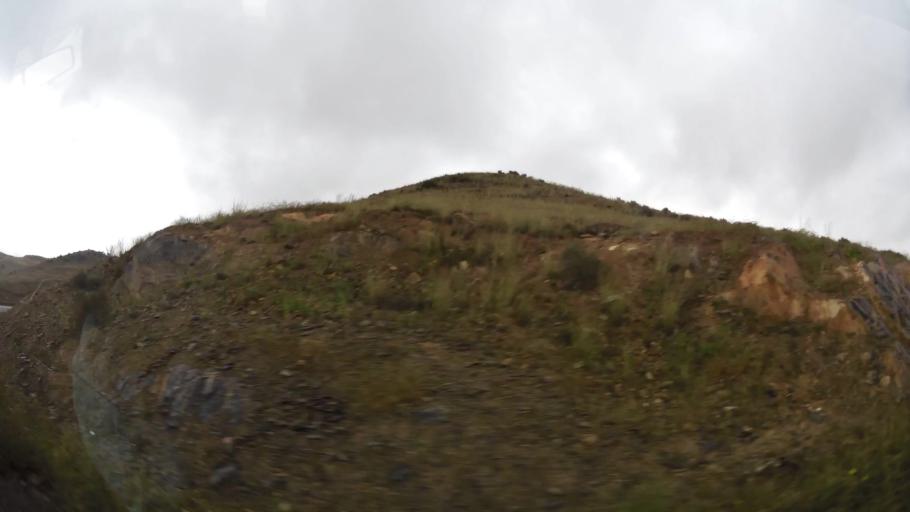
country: MA
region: Oriental
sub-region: Nador
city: Midar
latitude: 35.0658
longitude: -3.4792
